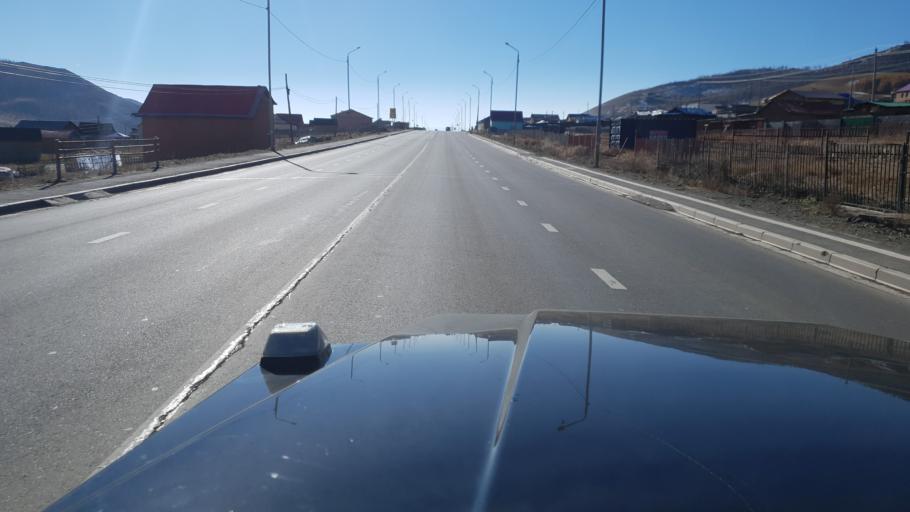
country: MN
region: Ulaanbaatar
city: Ulaanbaatar
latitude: 48.0421
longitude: 106.9037
